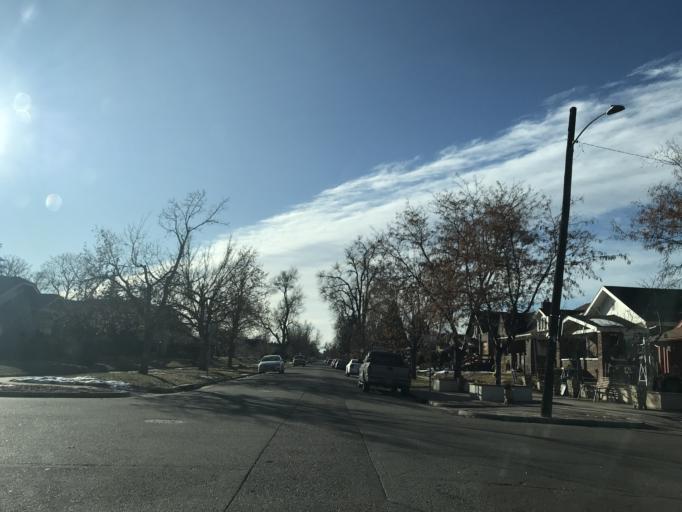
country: US
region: Colorado
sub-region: Denver County
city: Denver
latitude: 39.7671
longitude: -104.9623
